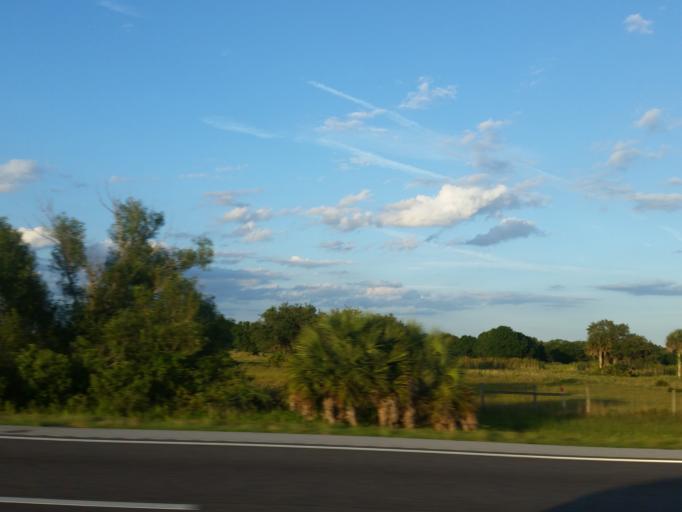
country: US
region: Florida
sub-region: Sarasota County
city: Laurel
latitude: 27.1729
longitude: -82.4338
